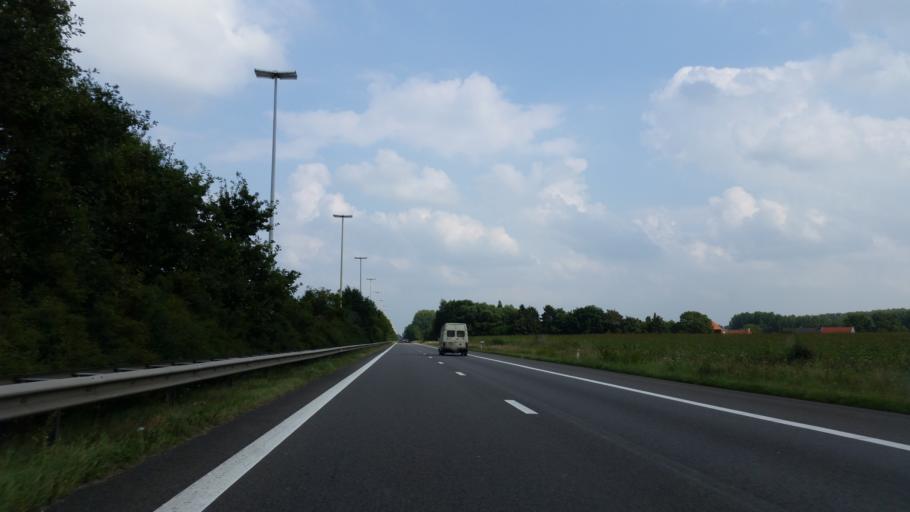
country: BE
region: Flanders
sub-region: Provincie Limburg
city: Kortessem
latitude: 50.8995
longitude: 5.3714
